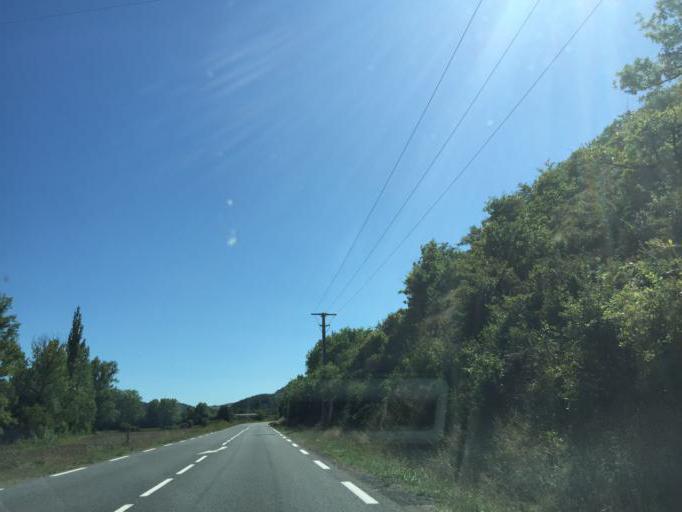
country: FR
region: Midi-Pyrenees
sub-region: Departement de l'Aveyron
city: Saint-Georges-de-Luzencon
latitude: 43.9969
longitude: 2.9697
